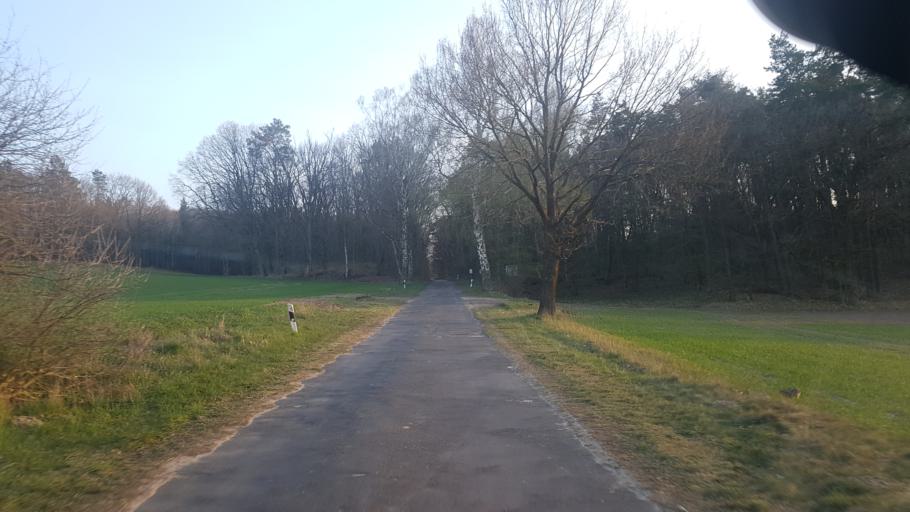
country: DE
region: Brandenburg
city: Gramzow
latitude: 53.2107
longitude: 13.9377
